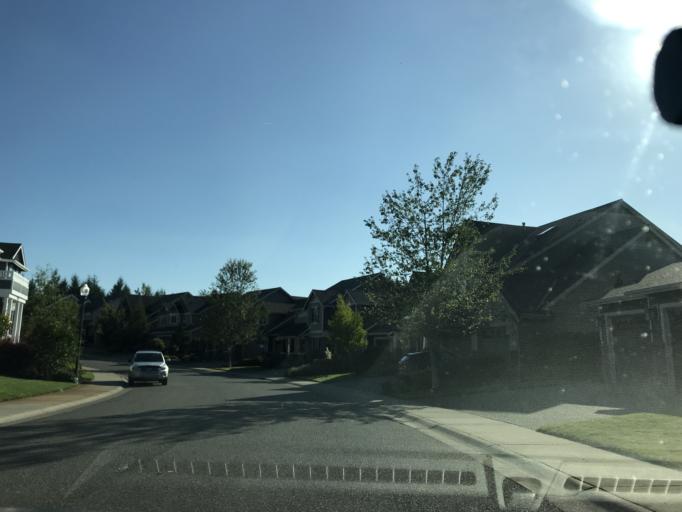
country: US
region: Washington
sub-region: King County
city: Ravensdale
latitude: 47.3558
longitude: -122.0038
